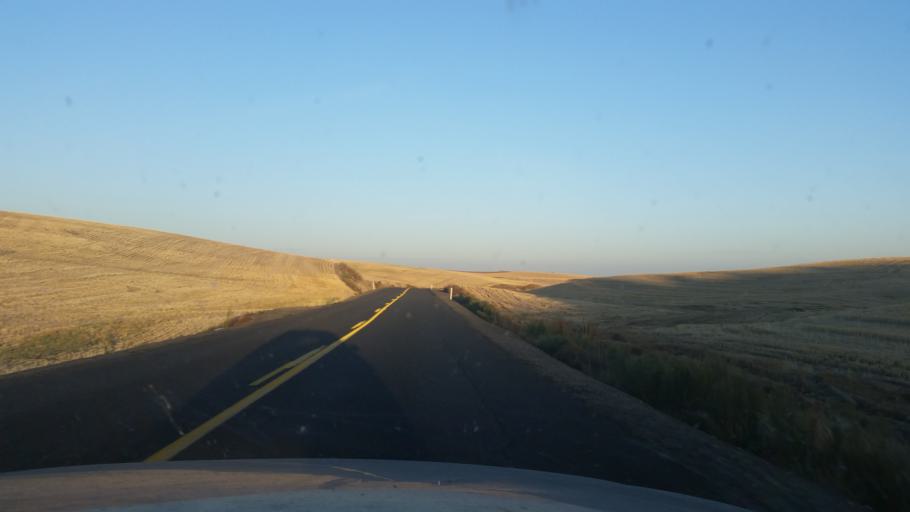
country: US
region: Washington
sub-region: Spokane County
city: Cheney
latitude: 47.5304
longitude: -117.6146
